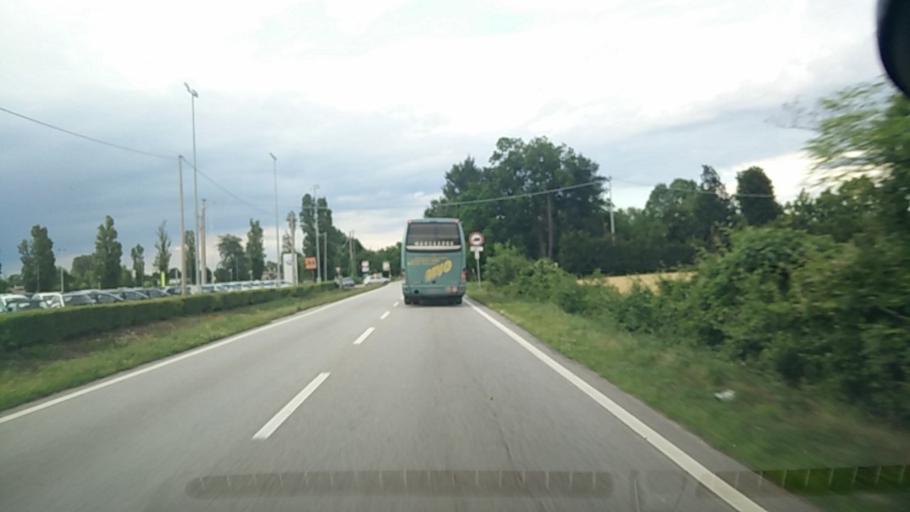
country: IT
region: Veneto
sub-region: Provincia di Venezia
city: Tessera
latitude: 45.4959
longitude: 12.3145
